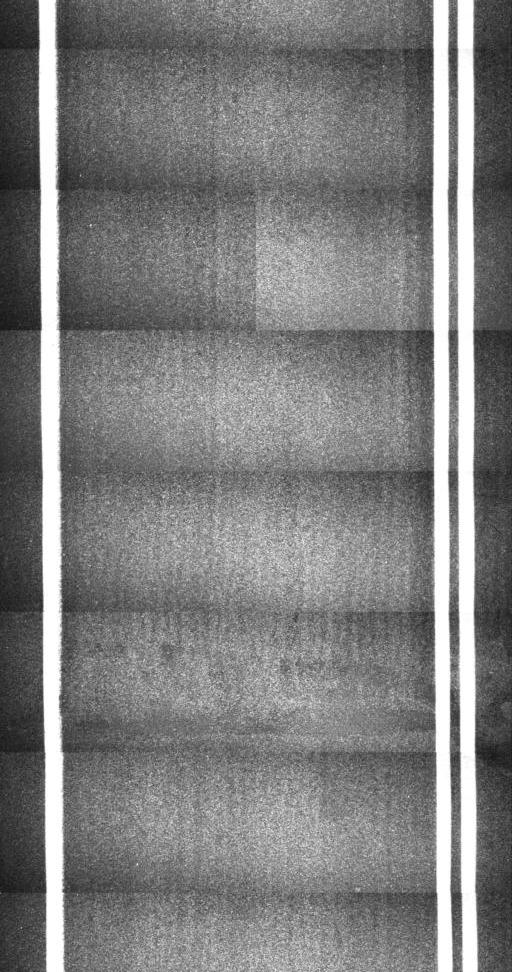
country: US
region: Vermont
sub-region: Windham County
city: Dover
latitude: 42.9931
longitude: -72.8885
